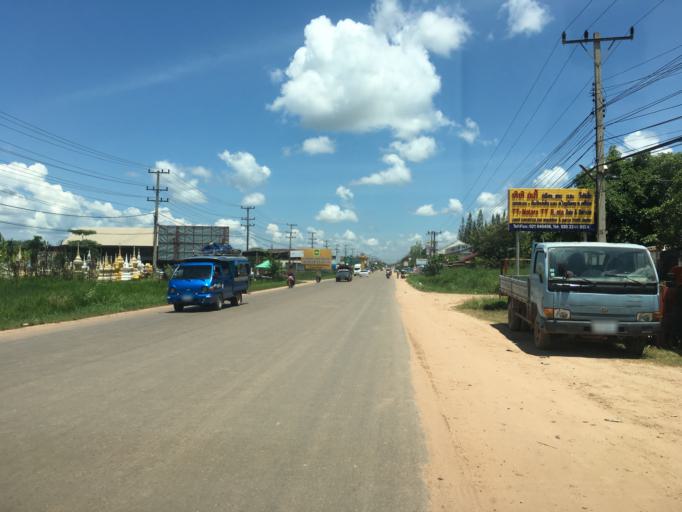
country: LA
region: Vientiane
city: Vientiane
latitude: 18.0337
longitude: 102.5479
